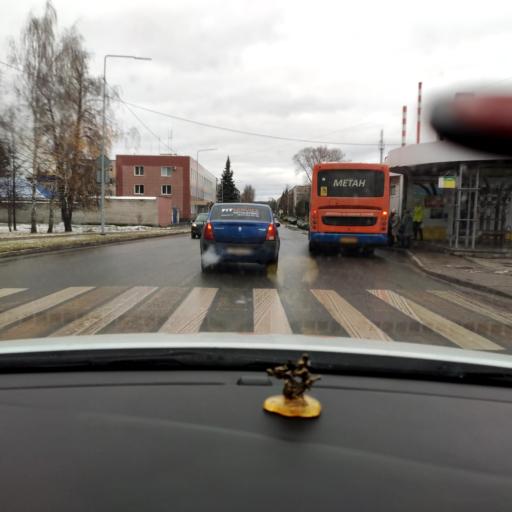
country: RU
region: Tatarstan
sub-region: Zelenodol'skiy Rayon
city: Zelenodolsk
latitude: 55.8459
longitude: 48.5240
